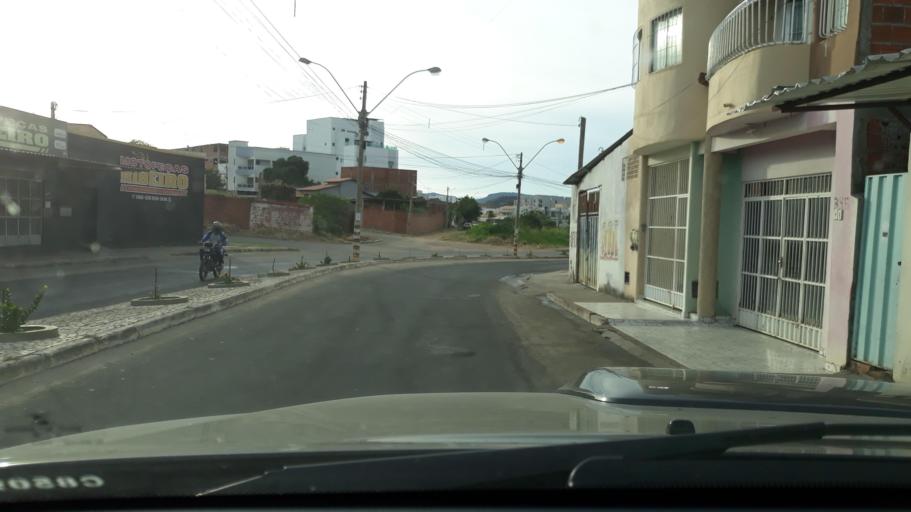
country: BR
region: Bahia
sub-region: Guanambi
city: Guanambi
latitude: -14.2315
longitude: -42.7778
